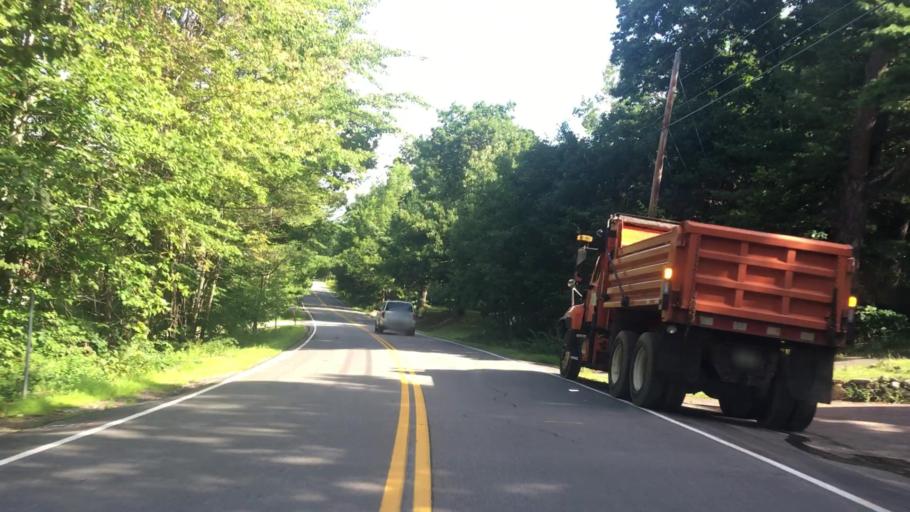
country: US
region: New Hampshire
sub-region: Belknap County
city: Gilford
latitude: 43.5358
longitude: -71.3470
